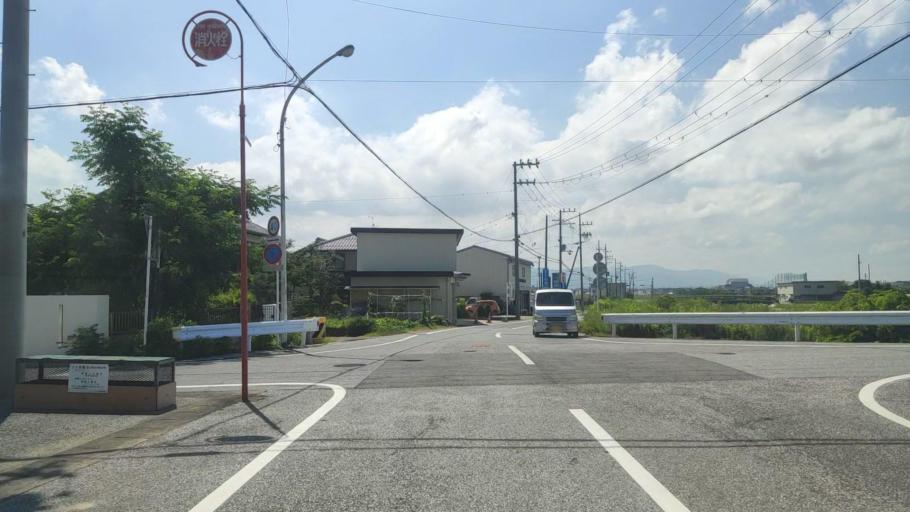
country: JP
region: Shiga Prefecture
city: Hikone
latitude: 35.2691
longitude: 136.2274
